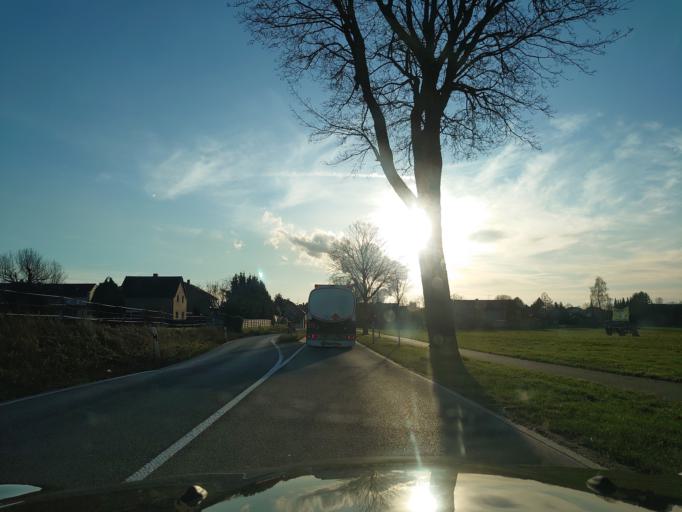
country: DE
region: North Rhine-Westphalia
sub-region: Regierungsbezirk Dusseldorf
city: Rommerskirchen
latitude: 51.0579
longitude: 6.7183
